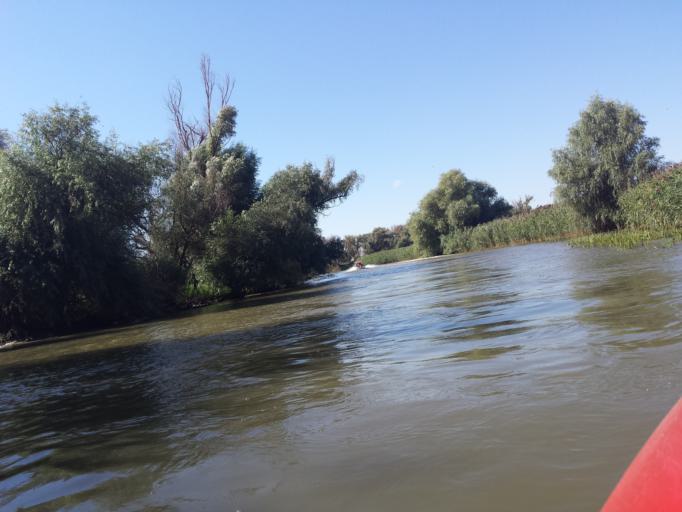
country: RO
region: Tulcea
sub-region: Comuna Pardina
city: Pardina
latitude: 45.2436
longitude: 29.0814
